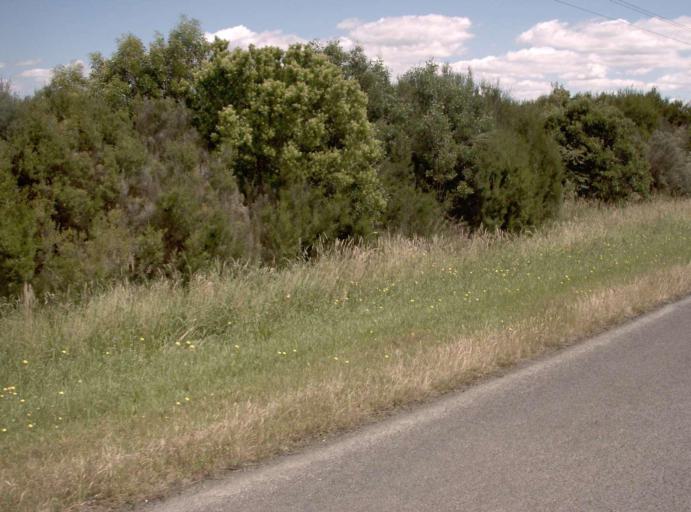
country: AU
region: Victoria
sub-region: Cardinia
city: Koo-Wee-Rup
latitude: -38.2984
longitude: 145.5436
